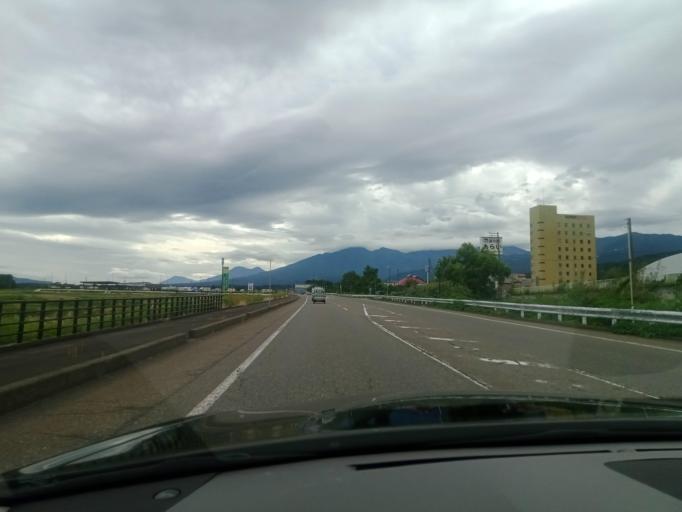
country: JP
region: Niigata
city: Arai
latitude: 37.0297
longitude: 138.2295
